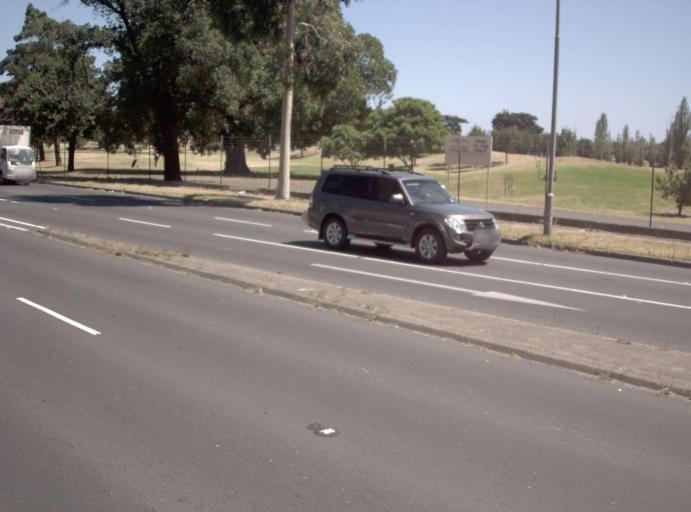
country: AU
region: Victoria
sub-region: Port Phillip
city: South Melbourne
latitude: -37.8365
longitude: 144.9733
